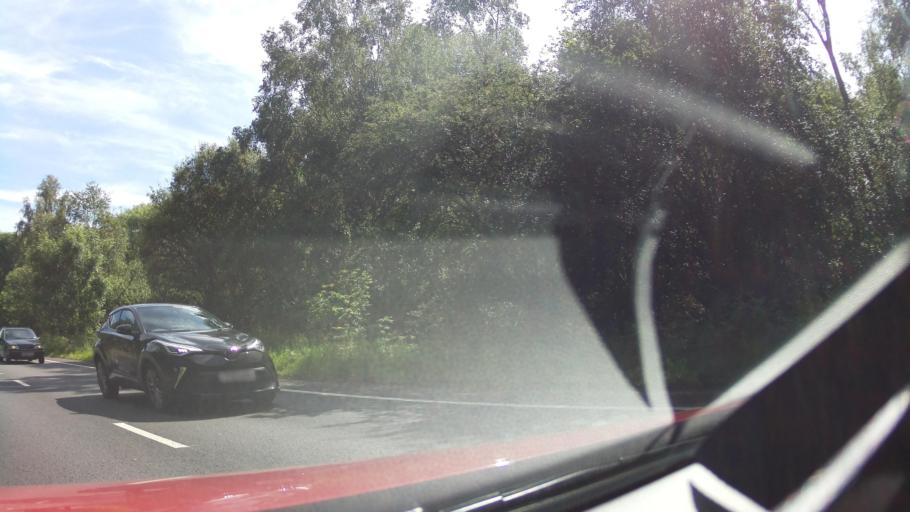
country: GB
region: England
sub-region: Lincolnshire
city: Skellingthorpe
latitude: 53.2251
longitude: -0.6054
